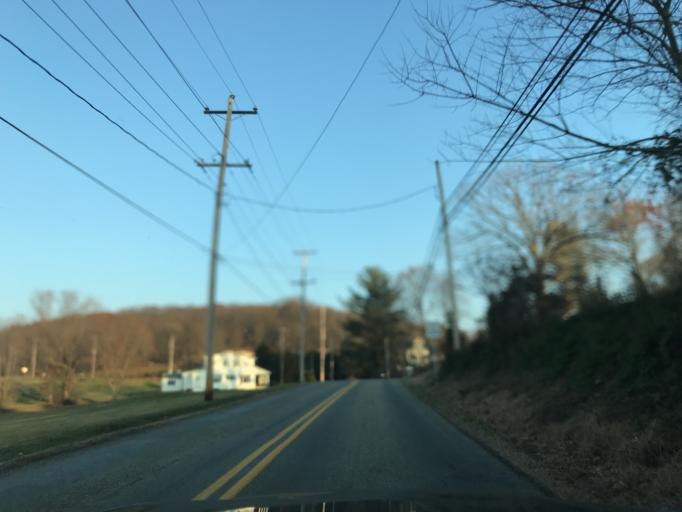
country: US
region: Pennsylvania
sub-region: York County
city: Susquehanna Trails
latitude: 39.6914
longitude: -76.3715
